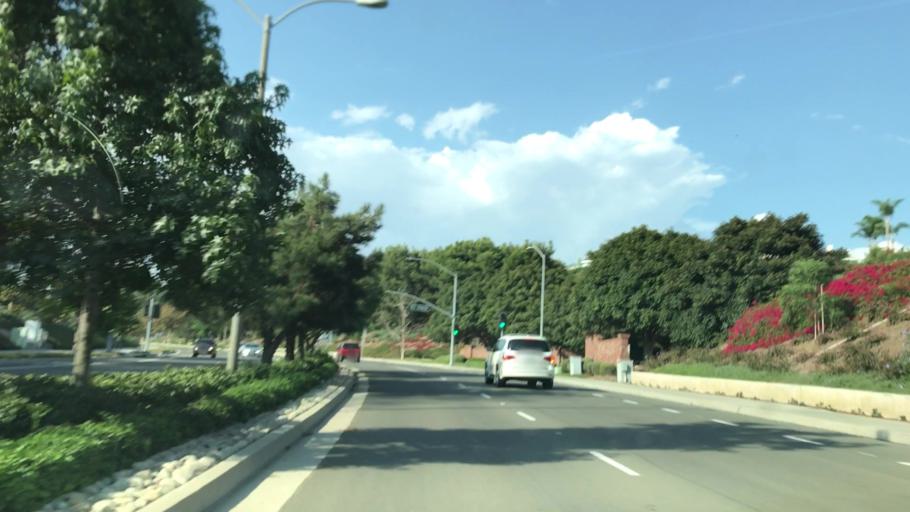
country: US
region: California
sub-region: Orange County
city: Dana Point
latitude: 33.4919
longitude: -117.7095
